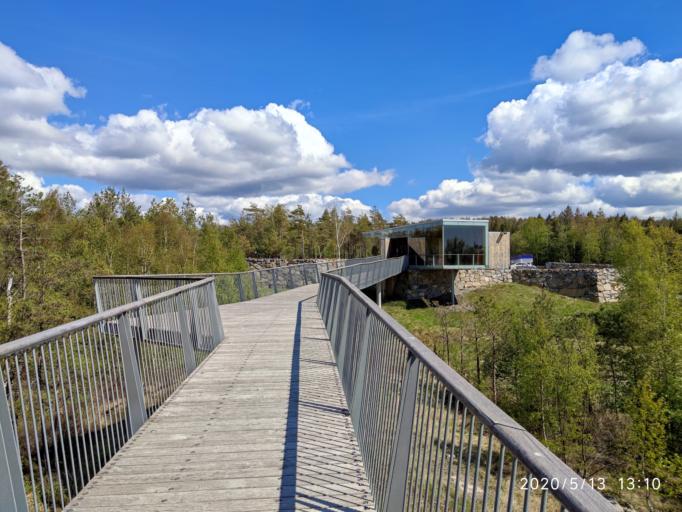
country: SE
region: Vaestra Goetaland
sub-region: Tanums Kommun
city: Tanumshede
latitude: 58.6976
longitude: 11.3870
